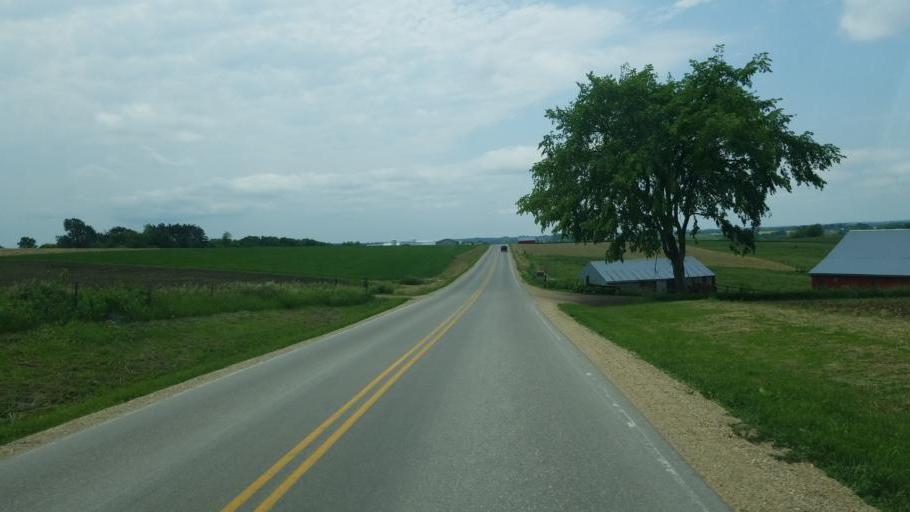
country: US
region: Wisconsin
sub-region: Monroe County
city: Cashton
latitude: 43.7148
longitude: -90.7222
